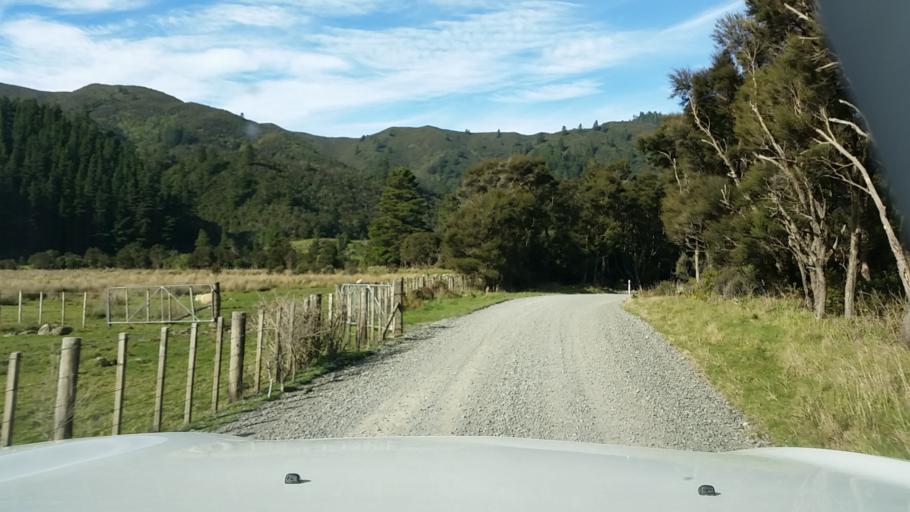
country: NZ
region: Wellington
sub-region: Masterton District
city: Masterton
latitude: -41.0113
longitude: 175.3953
